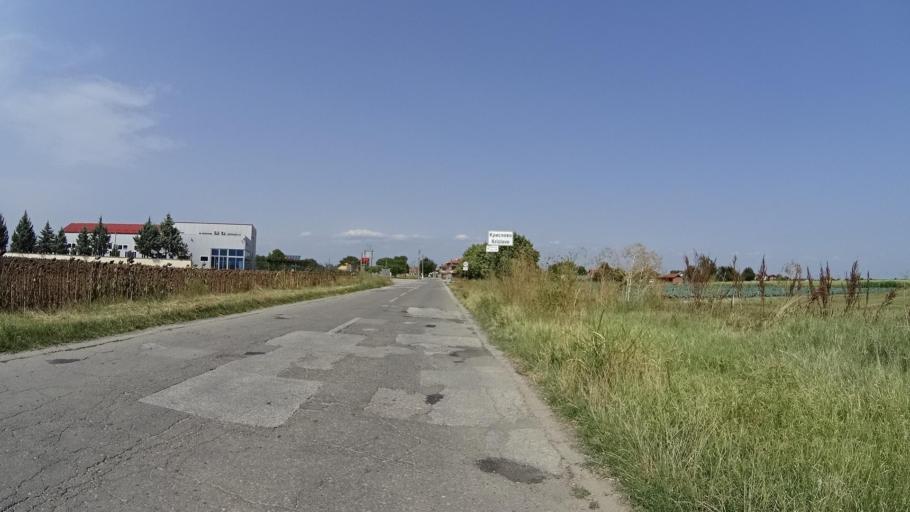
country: BG
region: Plovdiv
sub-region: Obshtina Plovdiv
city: Plovdiv
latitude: 42.2362
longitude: 24.7883
